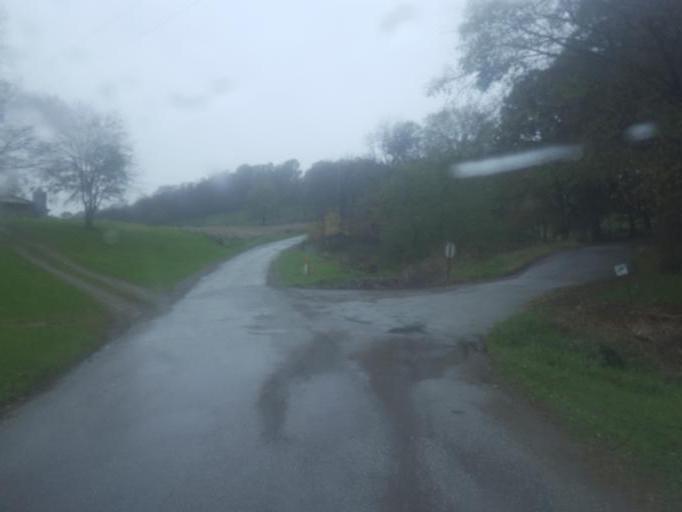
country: US
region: Ohio
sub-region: Holmes County
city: Millersburg
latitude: 40.5184
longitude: -81.9341
